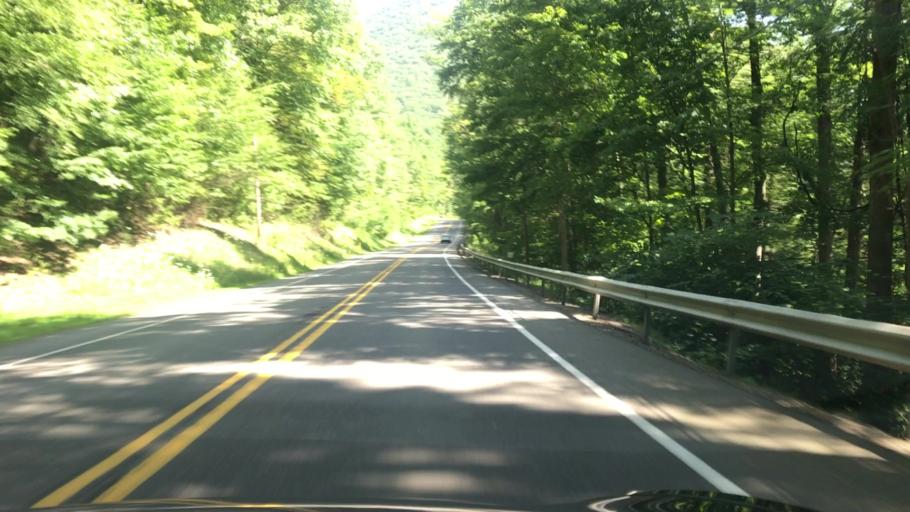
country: US
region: Pennsylvania
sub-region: Lycoming County
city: Garden View
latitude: 41.4106
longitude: -77.0443
